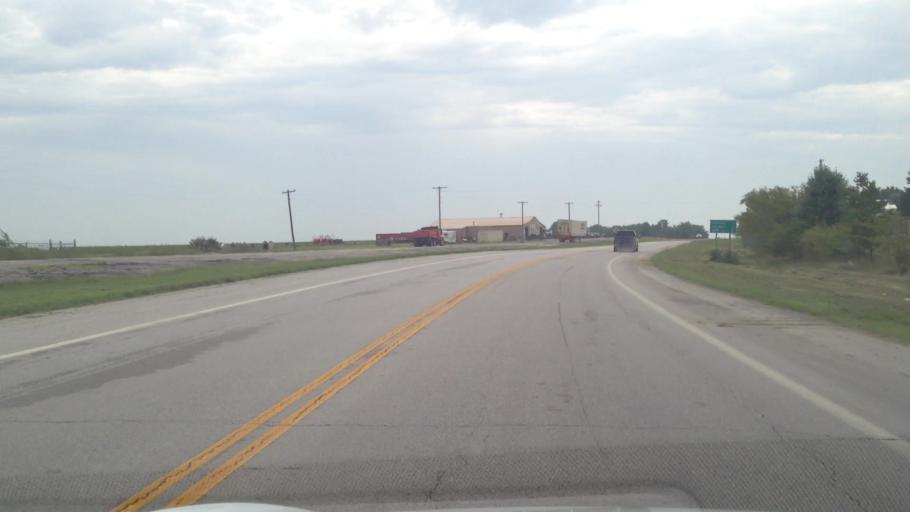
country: US
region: Kansas
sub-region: Crawford County
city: Girard
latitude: 37.4987
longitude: -94.8429
